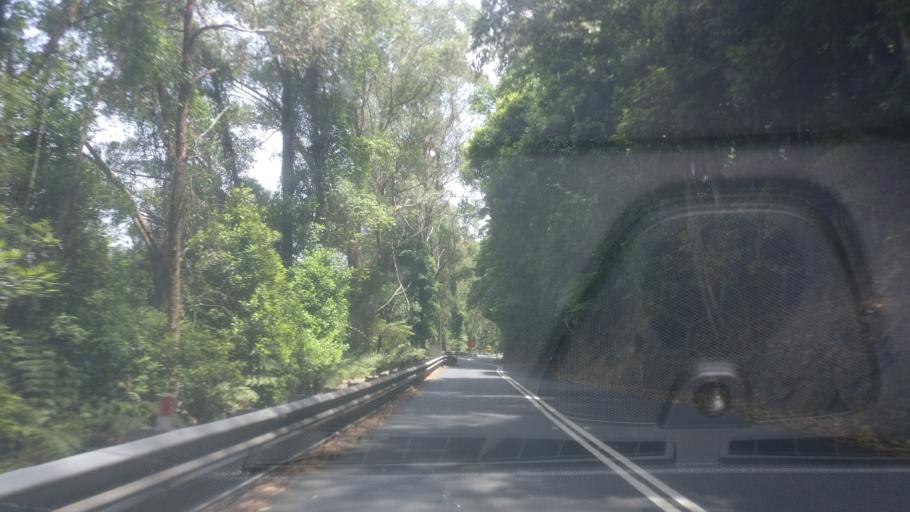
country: AU
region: New South Wales
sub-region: Shoalhaven Shire
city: Kangaroo Valley
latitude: -34.7902
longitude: 150.5620
